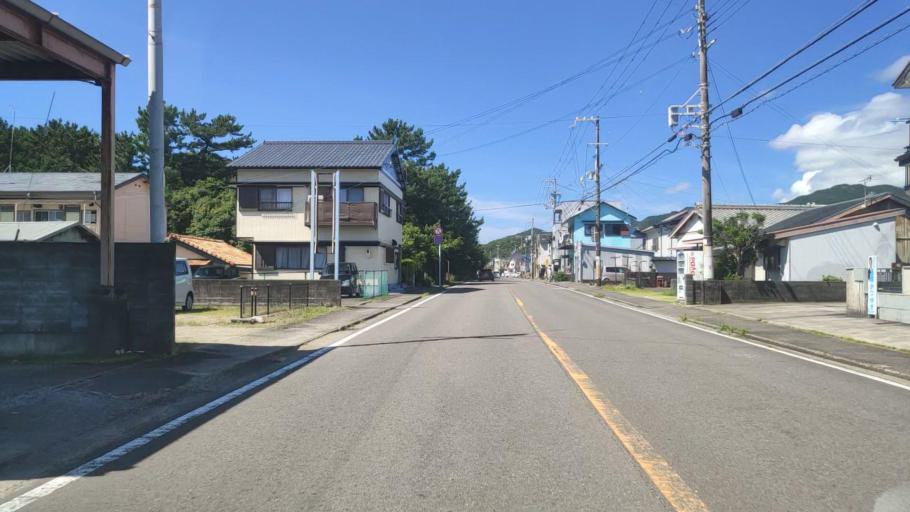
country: JP
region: Wakayama
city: Shingu
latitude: 33.7176
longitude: 136.0040
